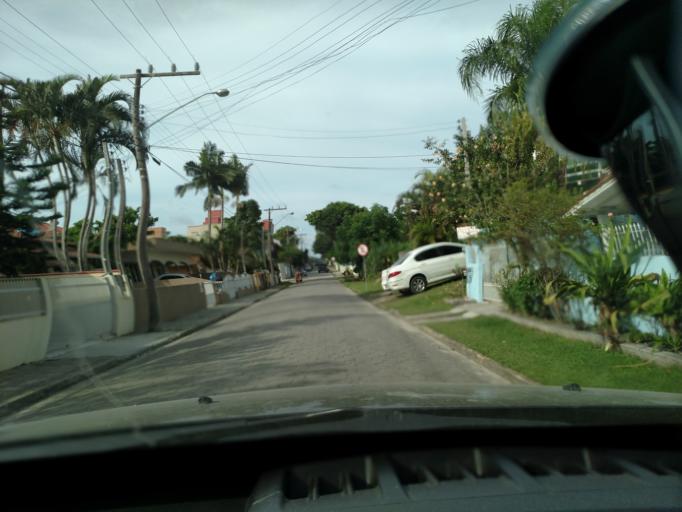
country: BR
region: Santa Catarina
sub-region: Porto Belo
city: Porto Belo
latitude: -27.1543
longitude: -48.4875
